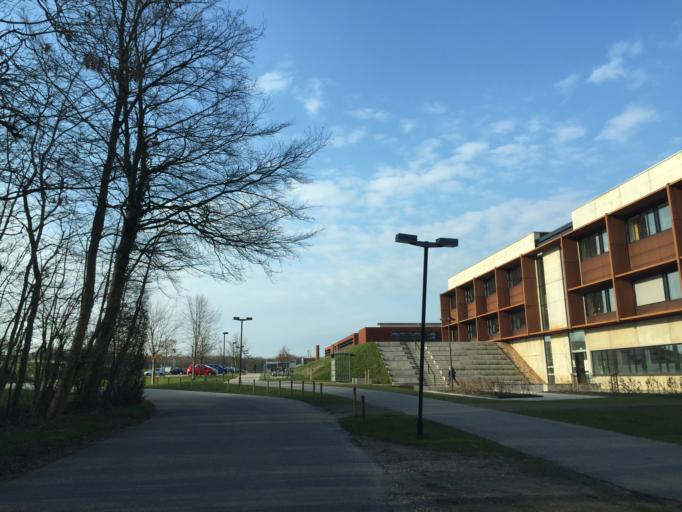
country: DK
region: South Denmark
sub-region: Odense Kommune
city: Neder Holluf
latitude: 55.3667
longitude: 10.4255
